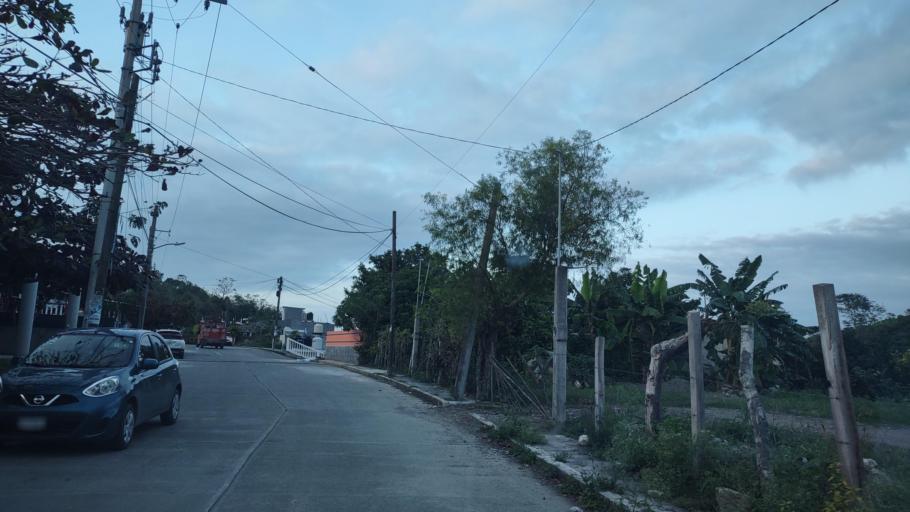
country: MX
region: Veracruz
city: Papantla de Olarte
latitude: 20.4590
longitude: -97.3069
